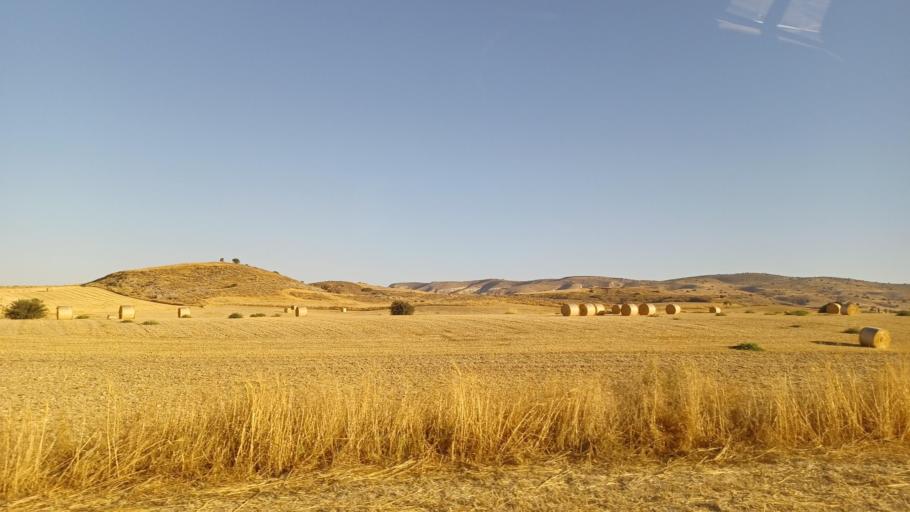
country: CY
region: Larnaka
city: Troulloi
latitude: 35.0237
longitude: 33.6475
